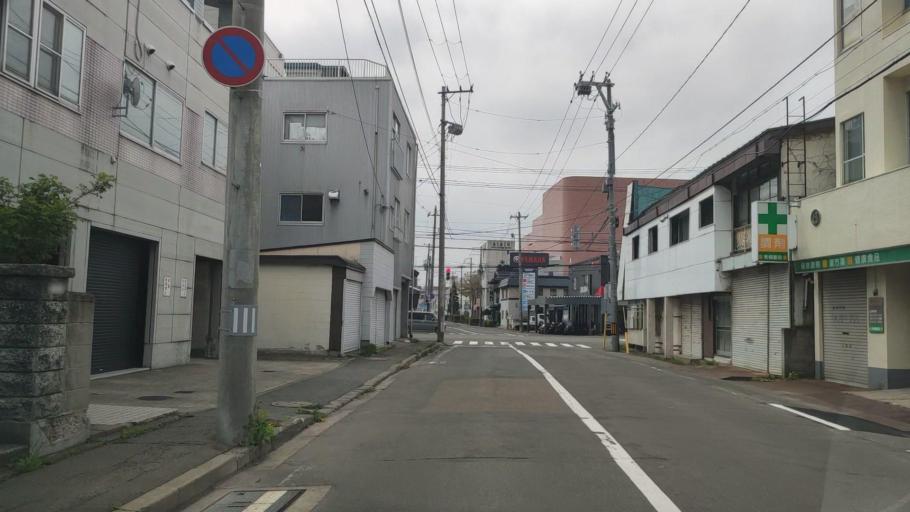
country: JP
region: Aomori
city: Aomori Shi
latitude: 40.8261
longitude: 140.7575
